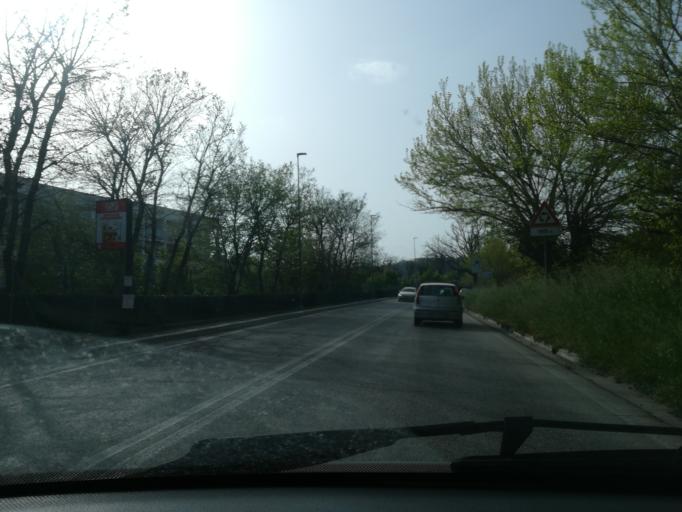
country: IT
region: The Marches
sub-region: Provincia di Macerata
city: Piediripa
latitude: 43.2877
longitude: 13.4743
